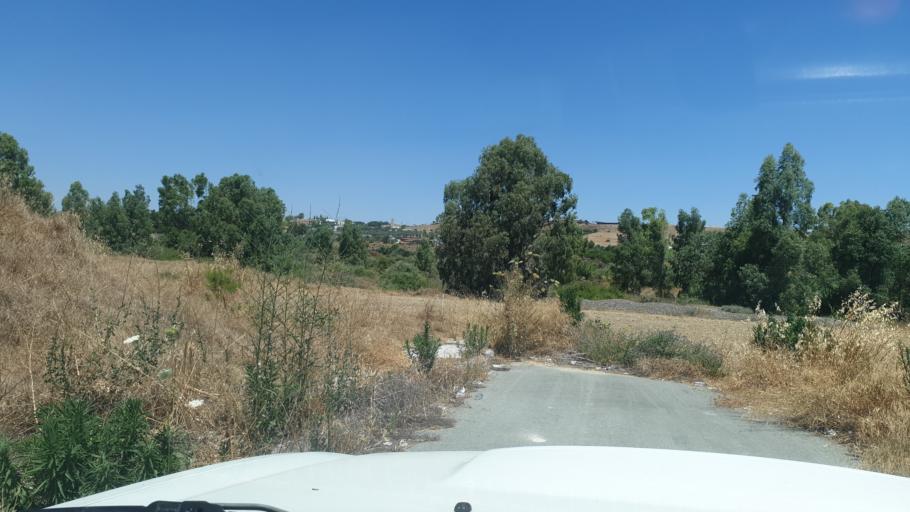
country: CY
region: Lefkosia
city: Dali
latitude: 35.0209
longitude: 33.4037
